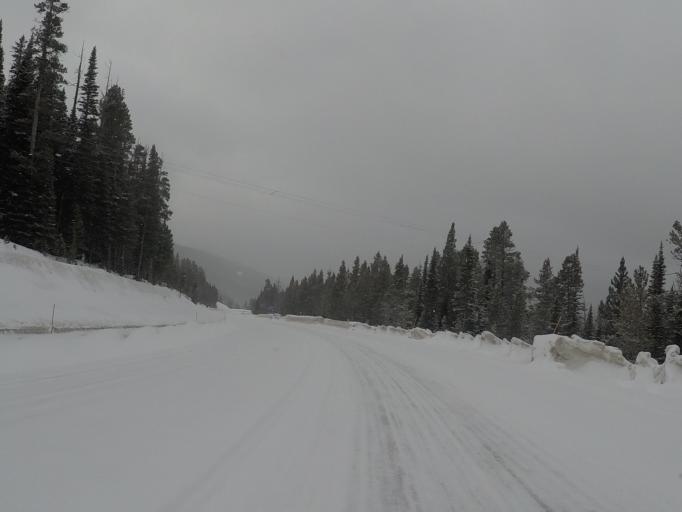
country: US
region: Montana
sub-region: Meagher County
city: White Sulphur Springs
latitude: 46.8398
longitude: -110.6961
